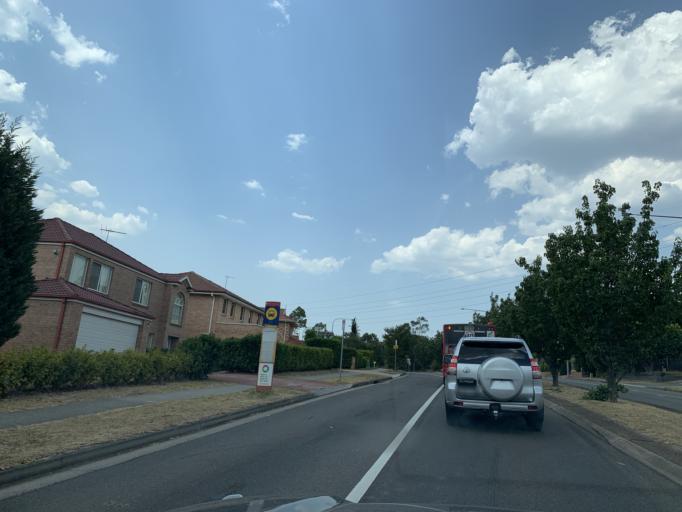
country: AU
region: New South Wales
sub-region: The Hills Shire
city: West Pennant
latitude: -33.7259
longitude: 151.0362
